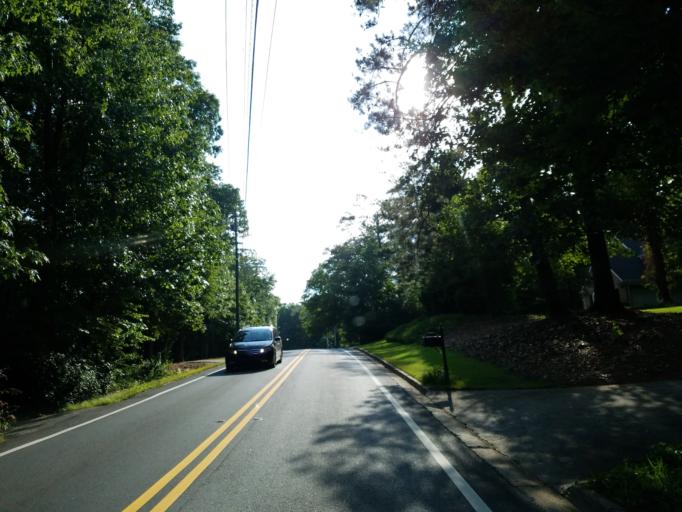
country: US
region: Georgia
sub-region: Fulton County
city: Roswell
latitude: 34.0048
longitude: -84.4382
